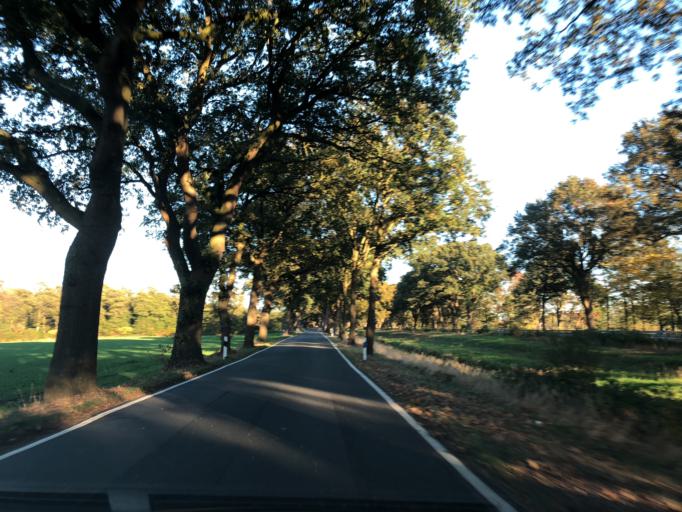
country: DE
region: Lower Saxony
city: Friesoythe
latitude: 53.0245
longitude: 7.8262
